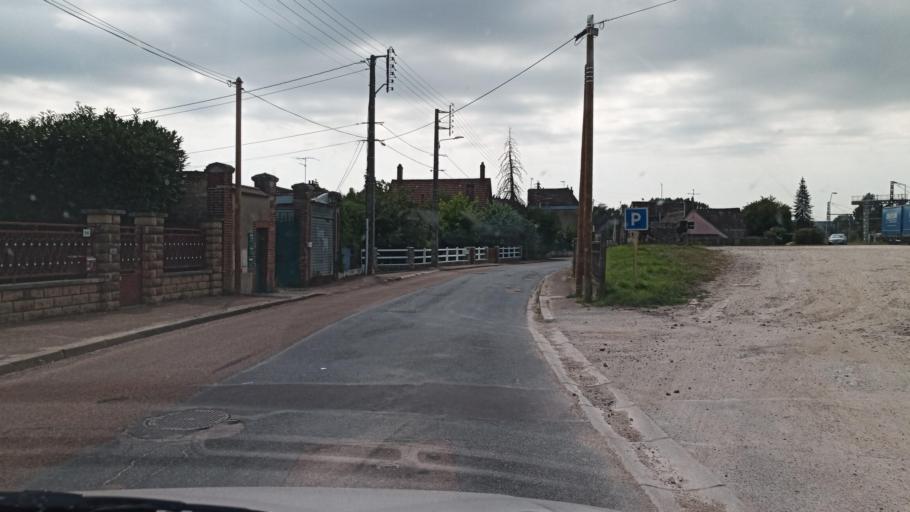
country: FR
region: Bourgogne
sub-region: Departement de l'Yonne
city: Villeneuve-sur-Yonne
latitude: 48.0849
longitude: 3.2872
